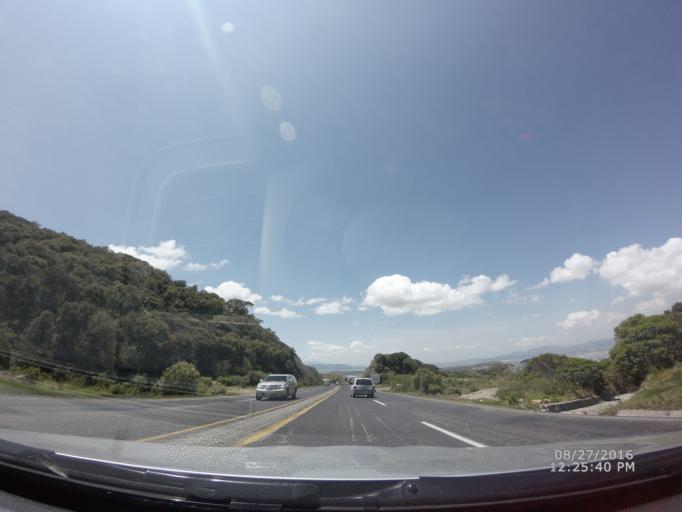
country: MX
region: Hidalgo
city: Mineral del Monte
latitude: 20.1330
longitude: -98.6922
